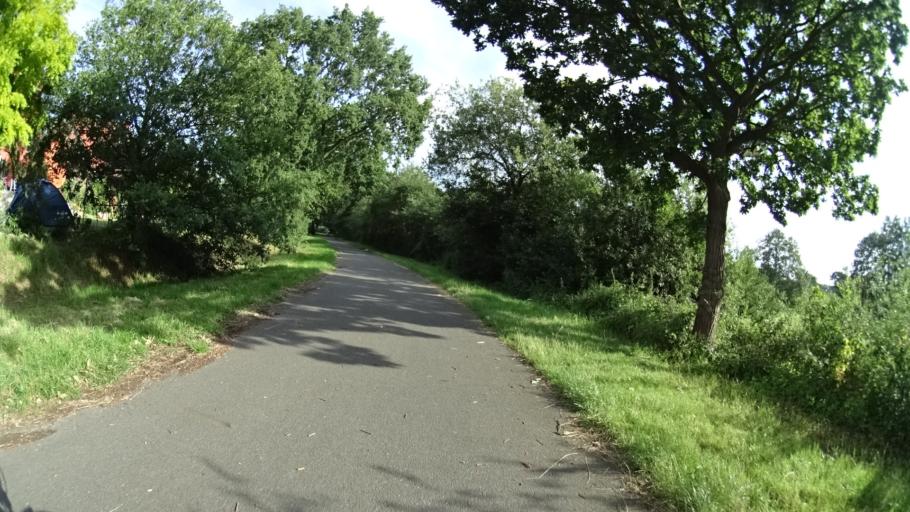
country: DE
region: Lower Saxony
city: Reppenstedt
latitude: 53.2448
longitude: 10.3585
